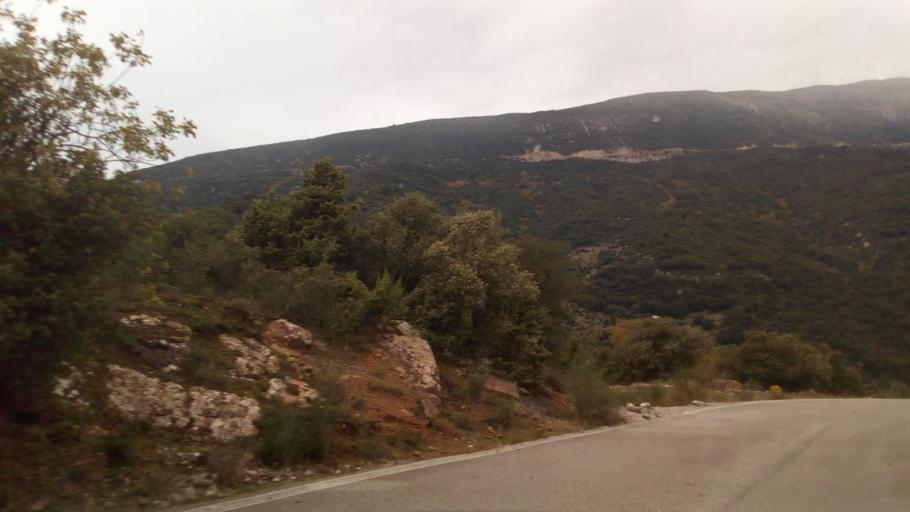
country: GR
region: West Greece
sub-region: Nomos Aitolias kai Akarnanias
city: Thermo
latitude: 38.5998
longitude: 21.8463
